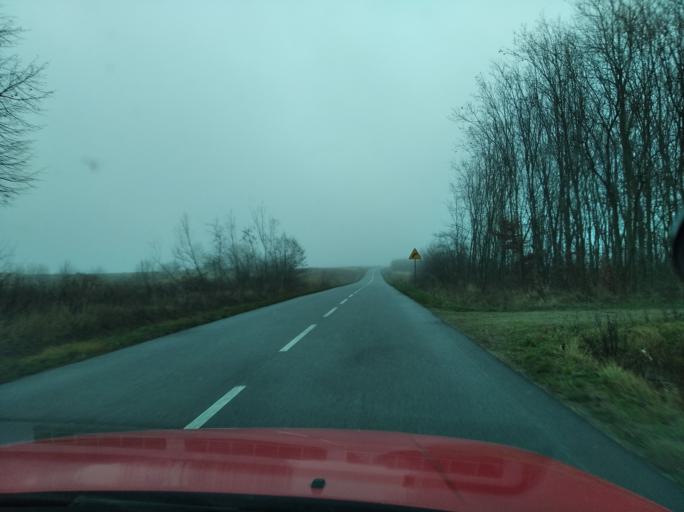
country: PL
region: Subcarpathian Voivodeship
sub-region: Powiat jaroslawski
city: Jodlowka
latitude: 49.8813
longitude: 22.4505
